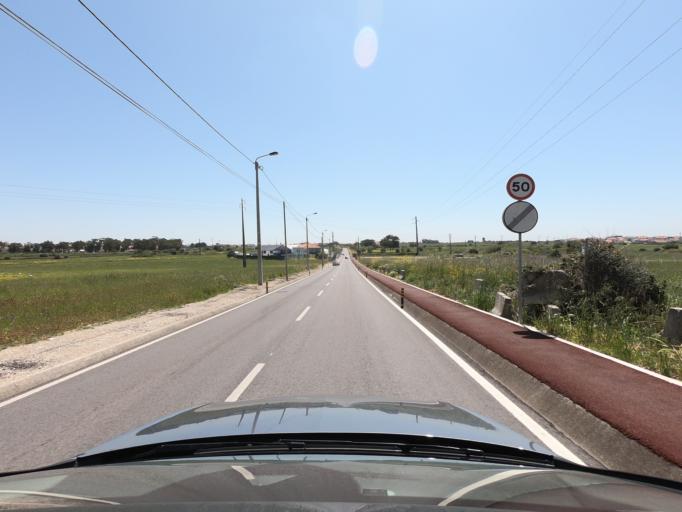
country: PT
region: Lisbon
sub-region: Cascais
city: Parede
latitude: 38.7361
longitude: -9.3548
